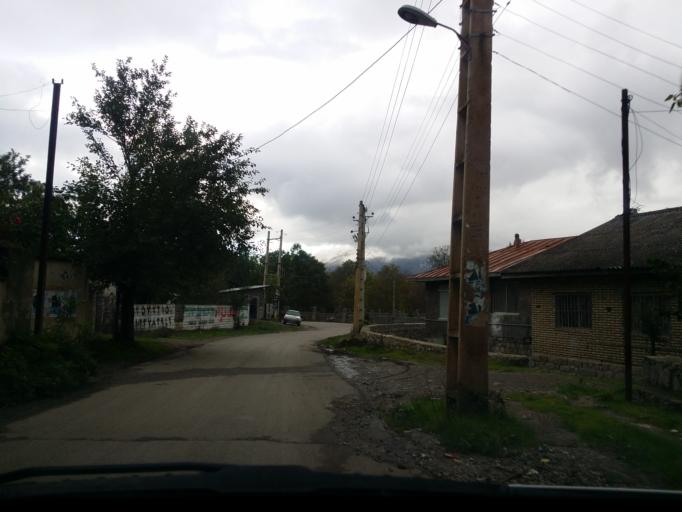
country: IR
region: Mazandaran
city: `Abbasabad
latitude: 36.5056
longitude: 51.1900
